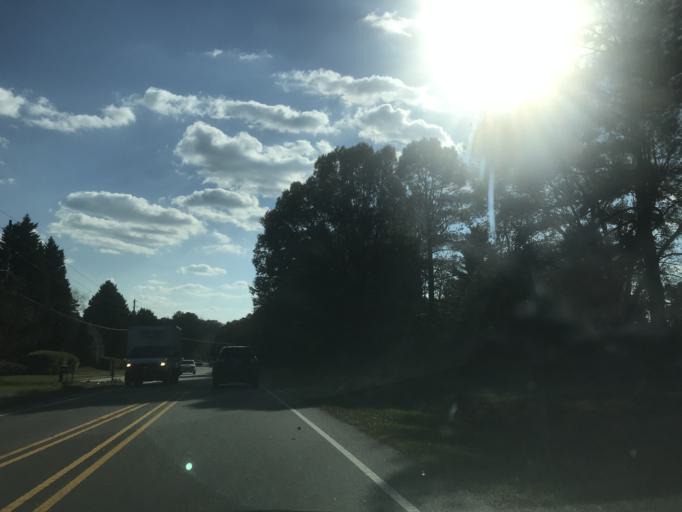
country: US
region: North Carolina
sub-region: Wake County
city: West Raleigh
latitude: 35.8803
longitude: -78.6617
